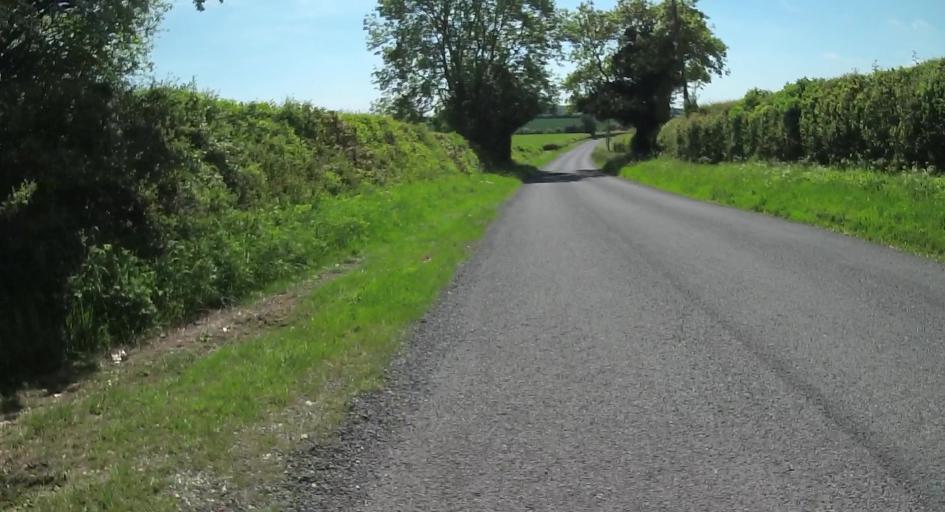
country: GB
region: England
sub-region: Hampshire
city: Four Marks
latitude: 51.1573
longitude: -1.1366
